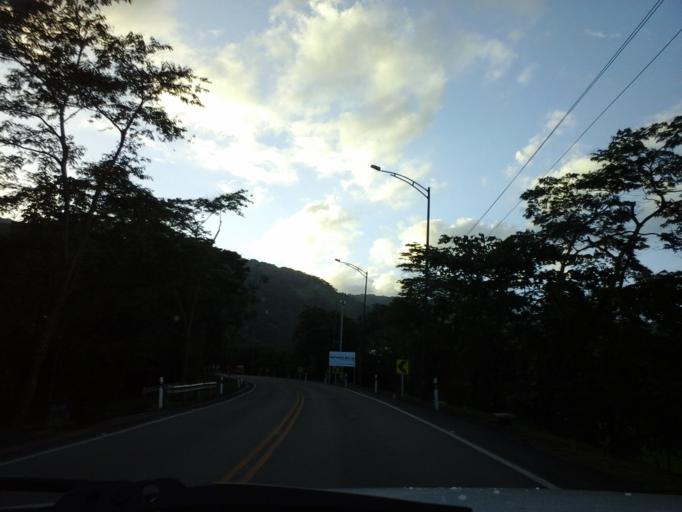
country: CO
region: Meta
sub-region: Villavicencio
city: Villavicencio
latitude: 4.1394
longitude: -73.6568
